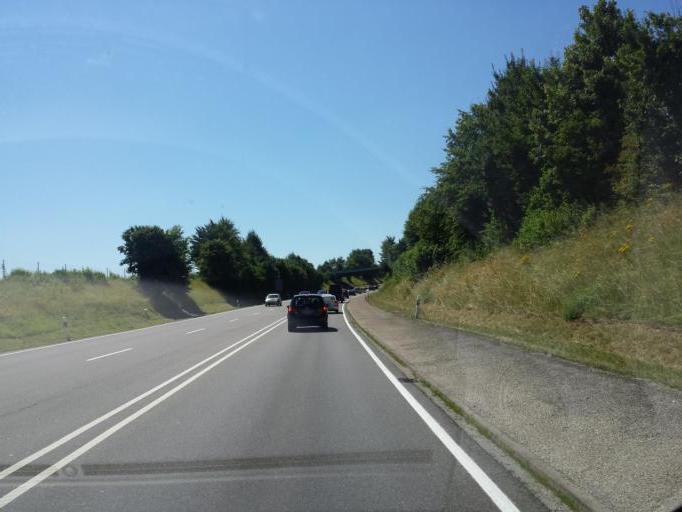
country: DE
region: Baden-Wuerttemberg
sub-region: Tuebingen Region
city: Owingen
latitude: 47.7928
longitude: 9.1507
